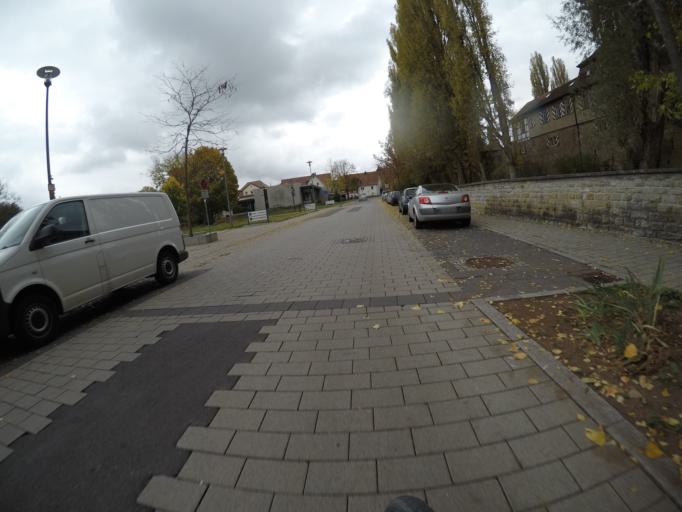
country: DE
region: Baden-Wuerttemberg
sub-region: Regierungsbezirk Stuttgart
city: Ehningen
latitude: 48.6575
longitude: 8.9447
